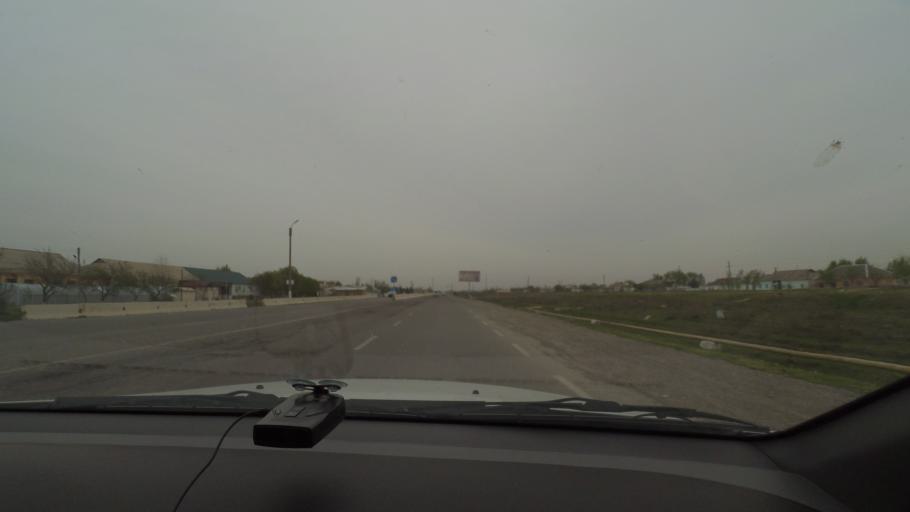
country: UZ
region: Sirdaryo
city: Guliston
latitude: 40.4917
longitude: 68.6969
